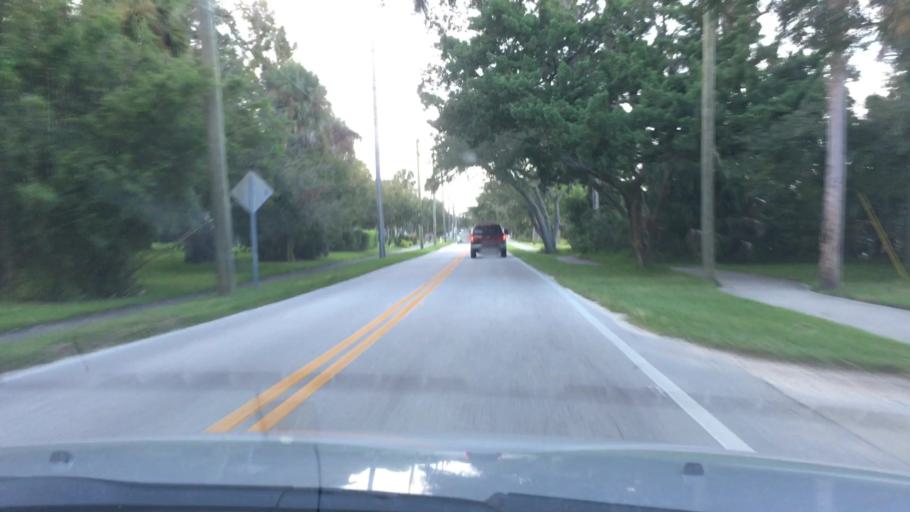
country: US
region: Florida
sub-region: Volusia County
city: Ormond Beach
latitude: 29.2815
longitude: -81.0536
